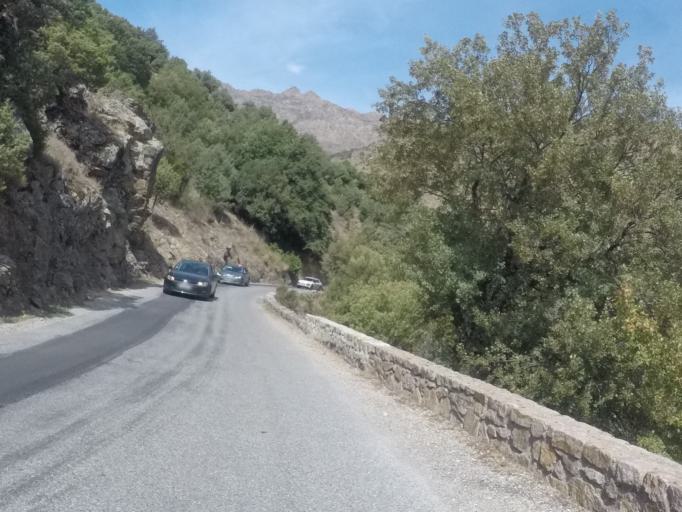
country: FR
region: Corsica
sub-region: Departement de la Haute-Corse
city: Corte
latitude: 42.3446
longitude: 9.0335
